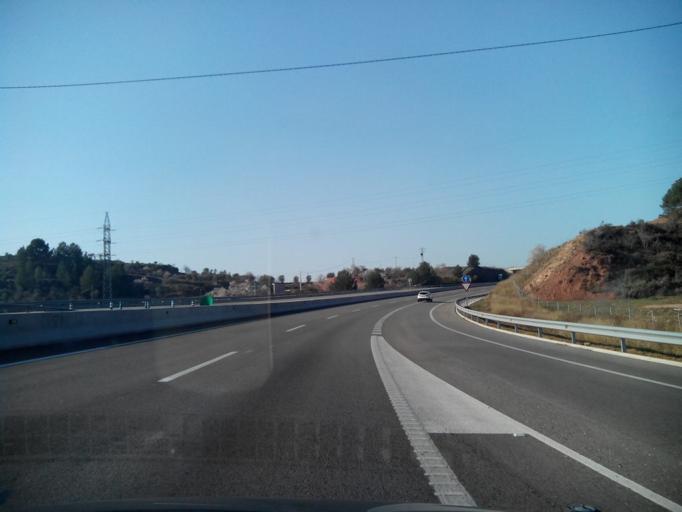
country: ES
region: Catalonia
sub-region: Provincia de Barcelona
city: Sant Joan de Vilatorrada
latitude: 41.7310
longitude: 1.8008
